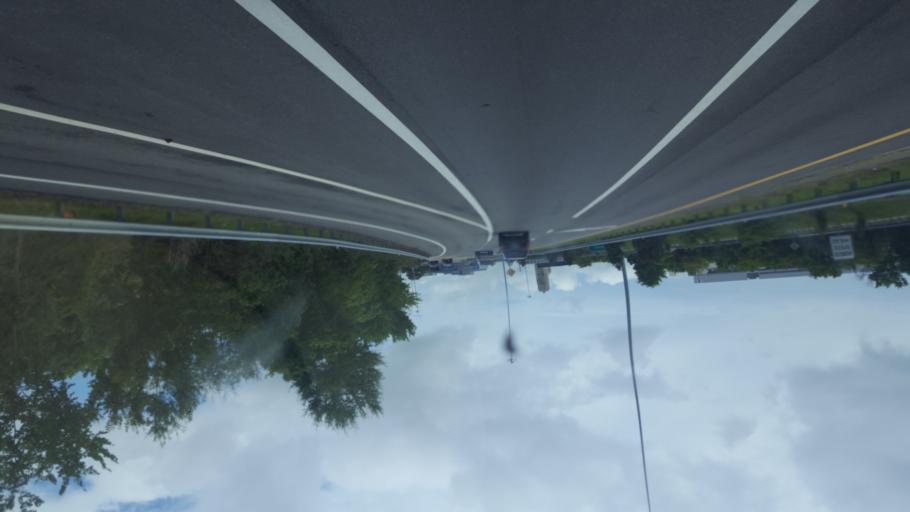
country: US
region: Virginia
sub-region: City of Richmond
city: Richmond
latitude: 37.5502
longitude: -77.4295
